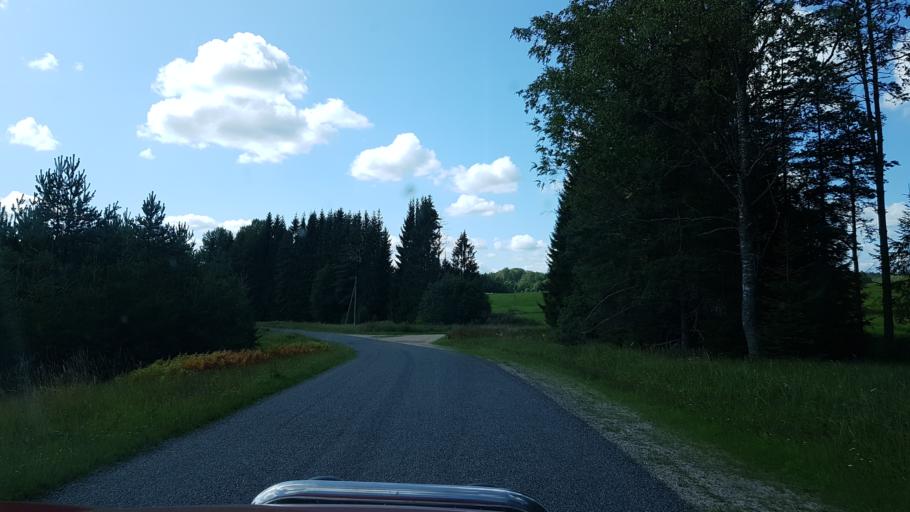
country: LV
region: Aluksnes Rajons
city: Aluksne
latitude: 57.6111
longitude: 27.1194
